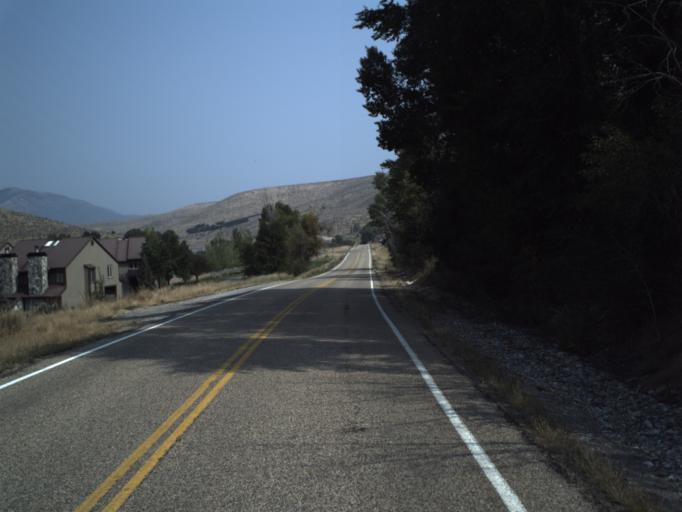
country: US
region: Utah
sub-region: Summit County
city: Summit Park
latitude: 40.8700
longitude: -111.5840
